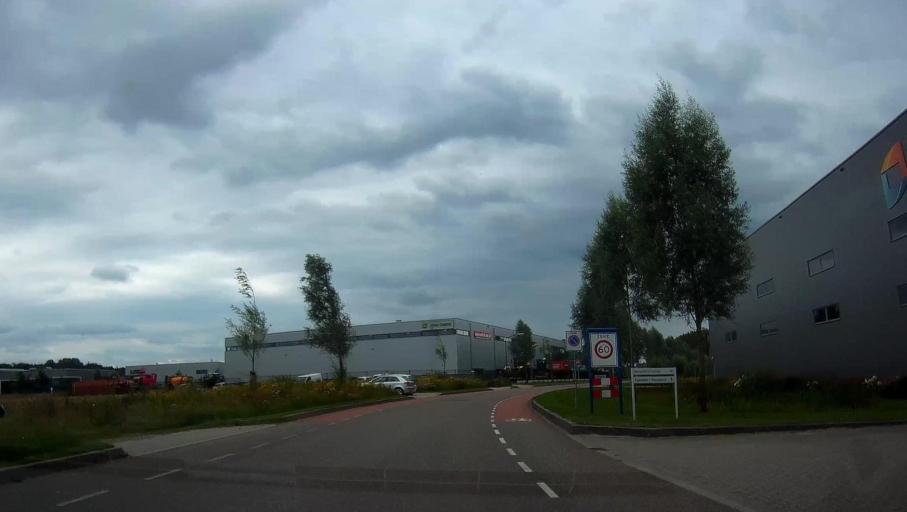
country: NL
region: North Brabant
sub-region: Gemeente Bladel en Netersel
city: Bladel
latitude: 51.3606
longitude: 5.1780
